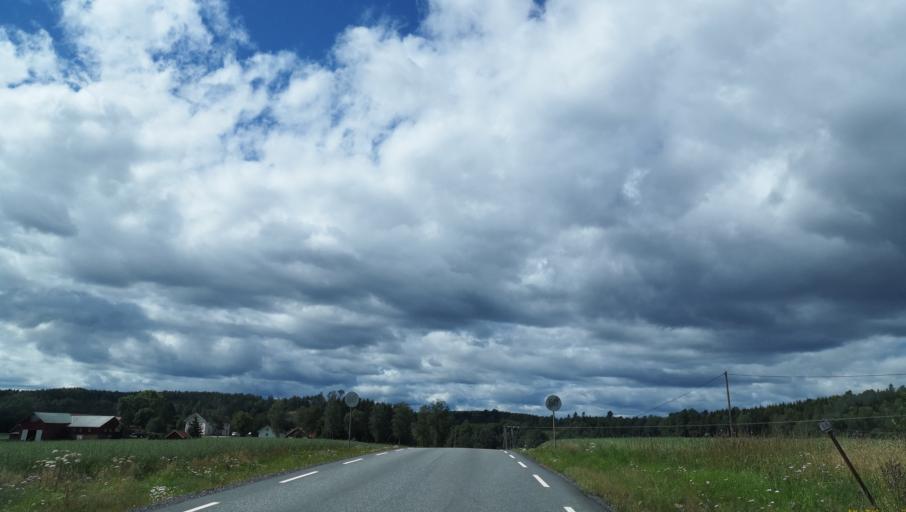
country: NO
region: Ostfold
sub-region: Hobol
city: Tomter
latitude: 59.6729
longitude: 11.0027
